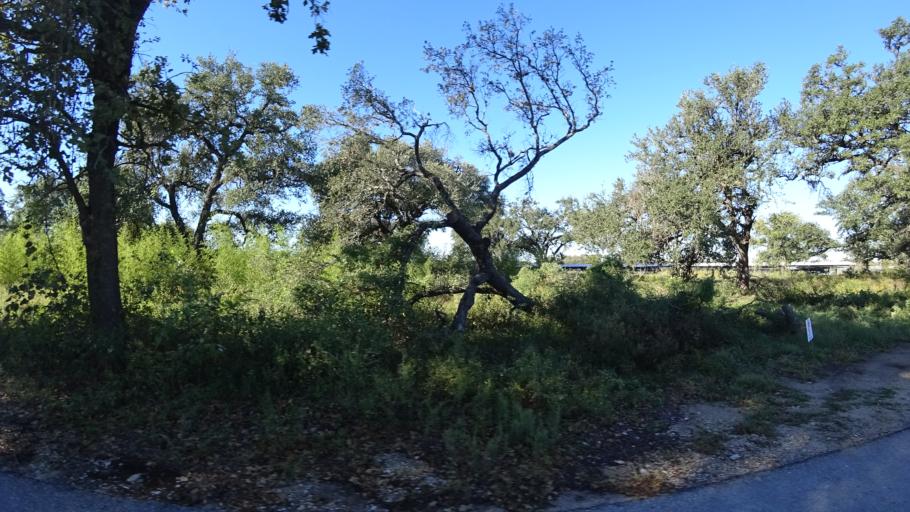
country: US
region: Texas
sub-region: Travis County
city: Hornsby Bend
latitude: 30.2202
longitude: -97.6613
